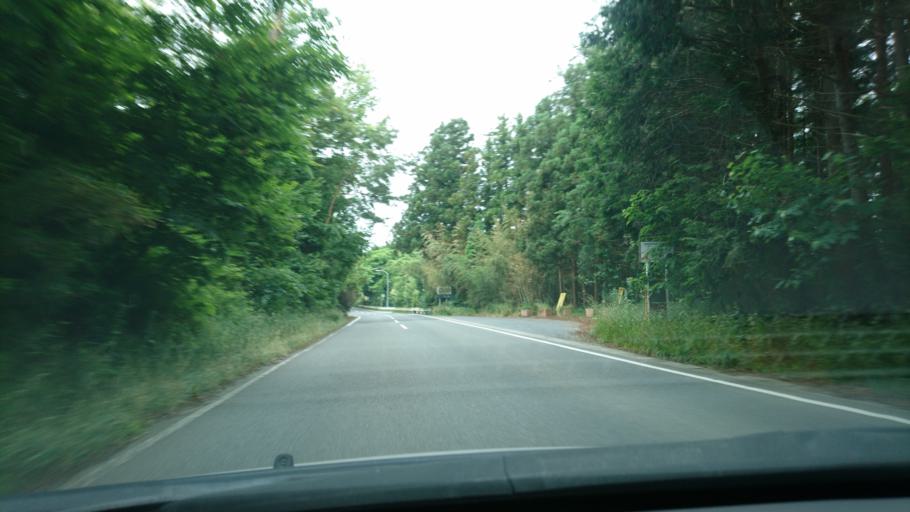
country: JP
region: Iwate
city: Ichinoseki
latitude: 38.7597
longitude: 141.2573
